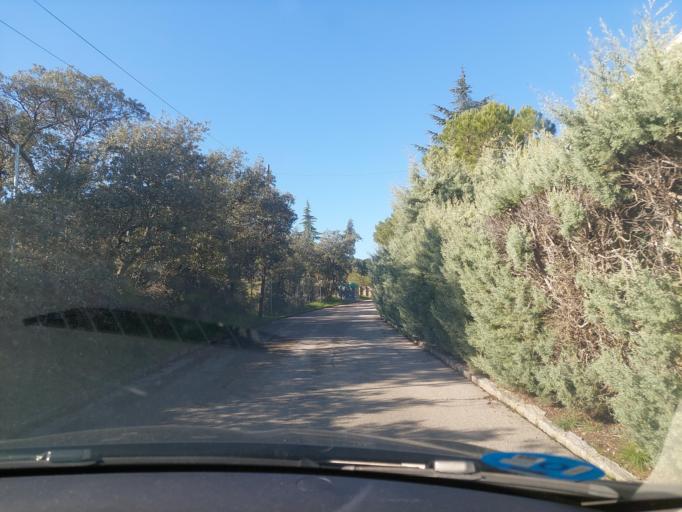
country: ES
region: Madrid
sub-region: Provincia de Madrid
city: Torrelodones
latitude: 40.5810
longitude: -3.9144
